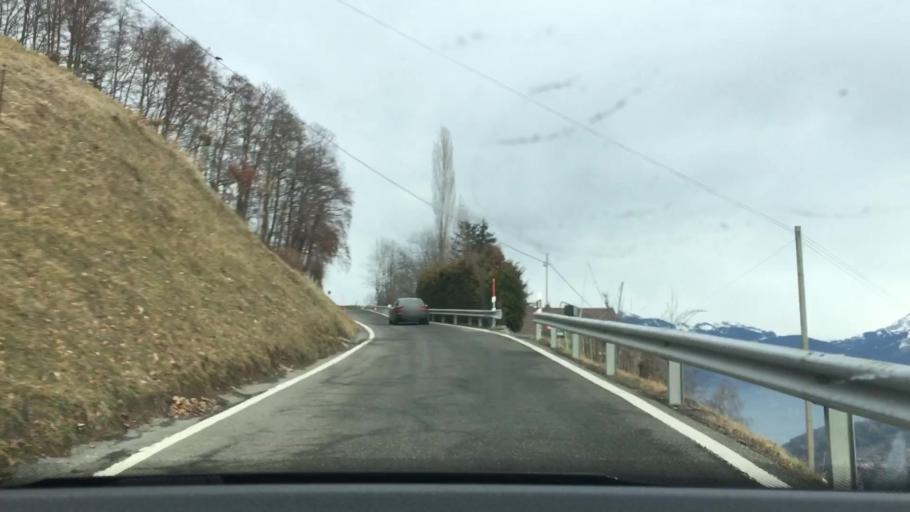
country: CH
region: Valais
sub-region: Monthey District
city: Troistorrents
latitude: 46.2254
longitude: 6.9087
